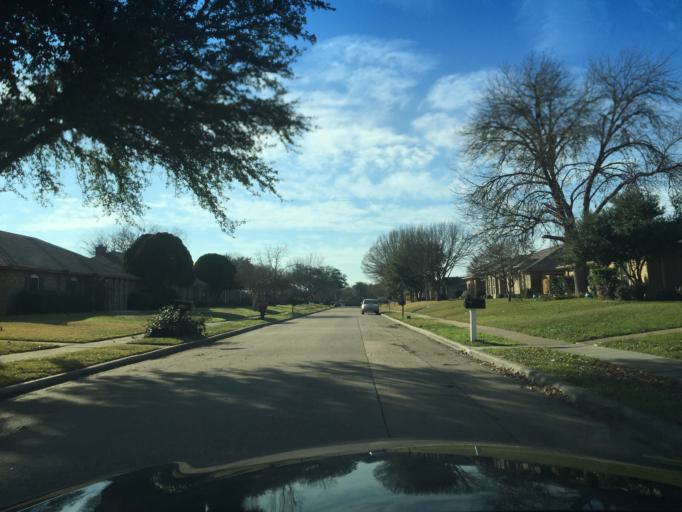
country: US
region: Texas
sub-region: Dallas County
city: Carrollton
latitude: 32.9804
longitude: -96.8797
